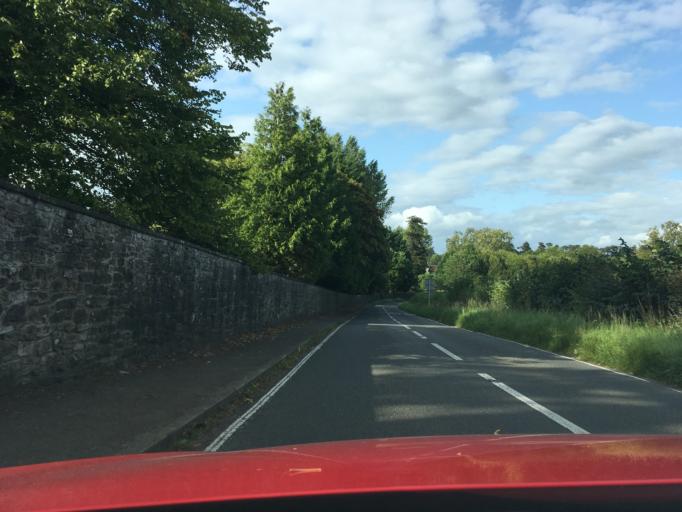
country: GB
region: England
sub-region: South Gloucestershire
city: Falfield
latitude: 51.6282
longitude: -2.4362
